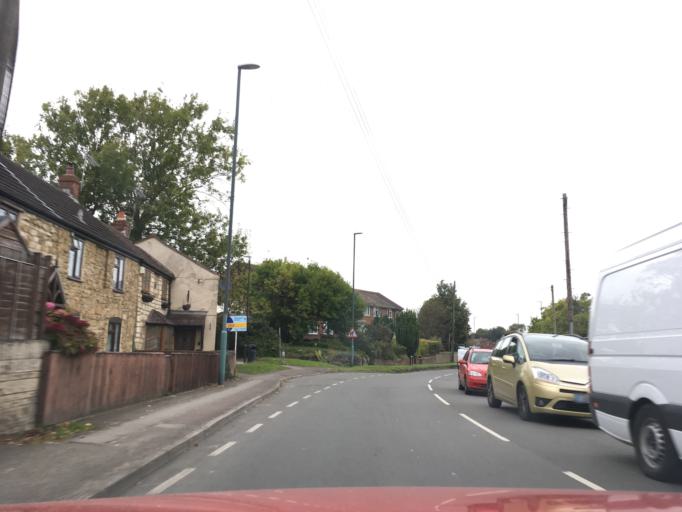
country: GB
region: England
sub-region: Gloucestershire
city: Dursley
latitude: 51.7050
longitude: -2.3665
